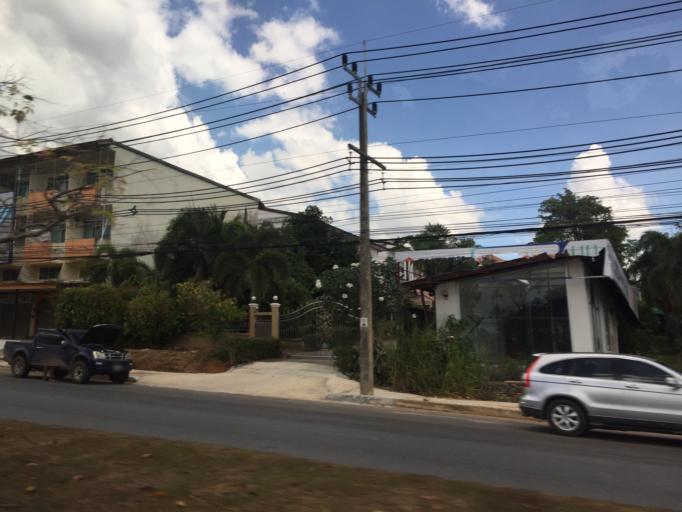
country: TH
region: Krabi
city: Krabi
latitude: 8.0901
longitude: 98.8920
